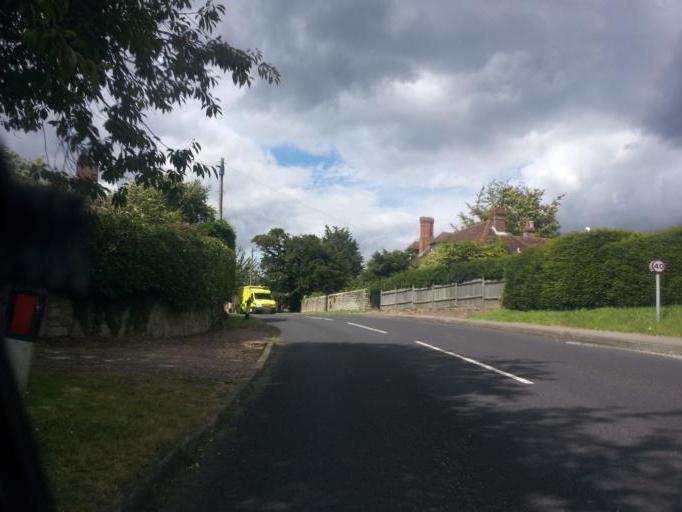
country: GB
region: England
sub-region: Kent
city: Wateringbury
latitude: 51.2610
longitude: 0.4313
